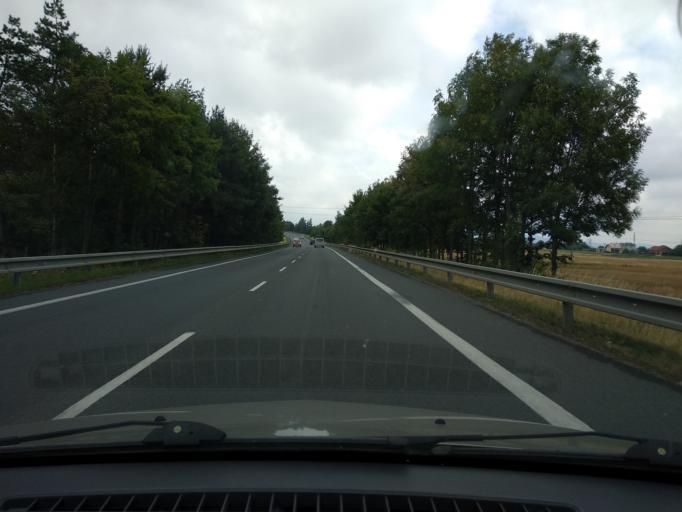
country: CZ
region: Olomoucky
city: Zabreh
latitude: 49.8824
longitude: 16.8933
